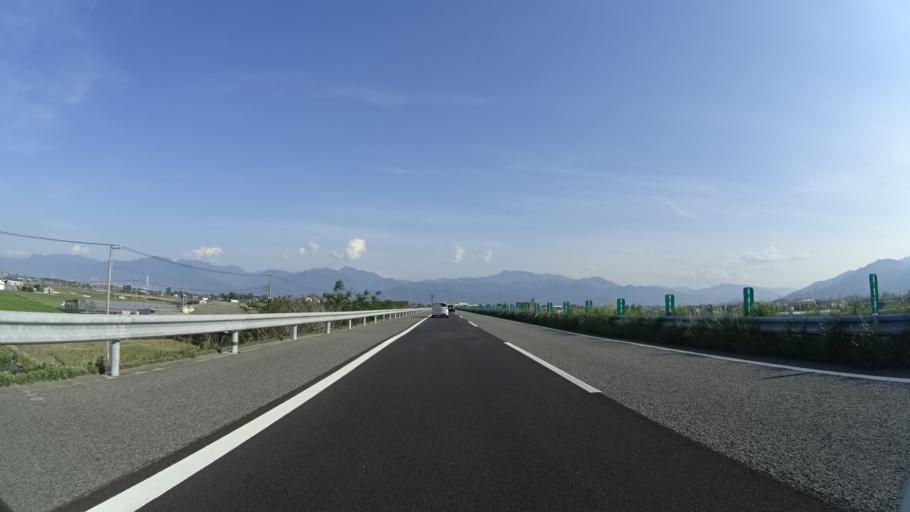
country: JP
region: Ehime
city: Saijo
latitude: 33.9576
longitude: 133.0661
